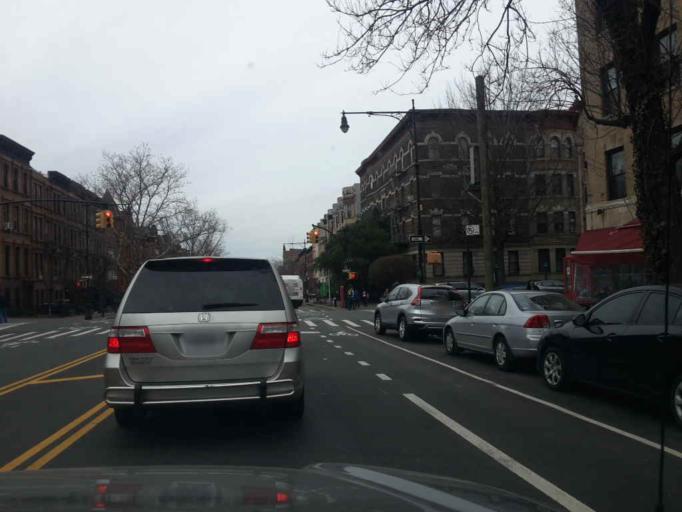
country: US
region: New York
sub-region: Kings County
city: Brooklyn
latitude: 40.6656
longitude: -73.9789
